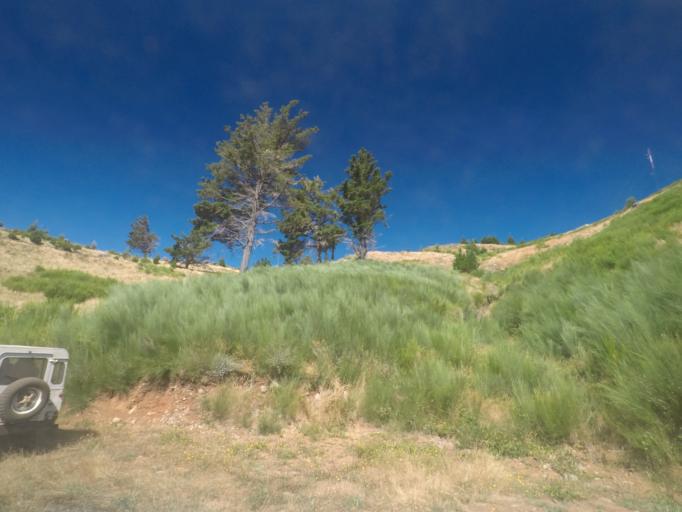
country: PT
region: Madeira
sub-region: Funchal
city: Nossa Senhora do Monte
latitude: 32.7078
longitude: -16.9065
